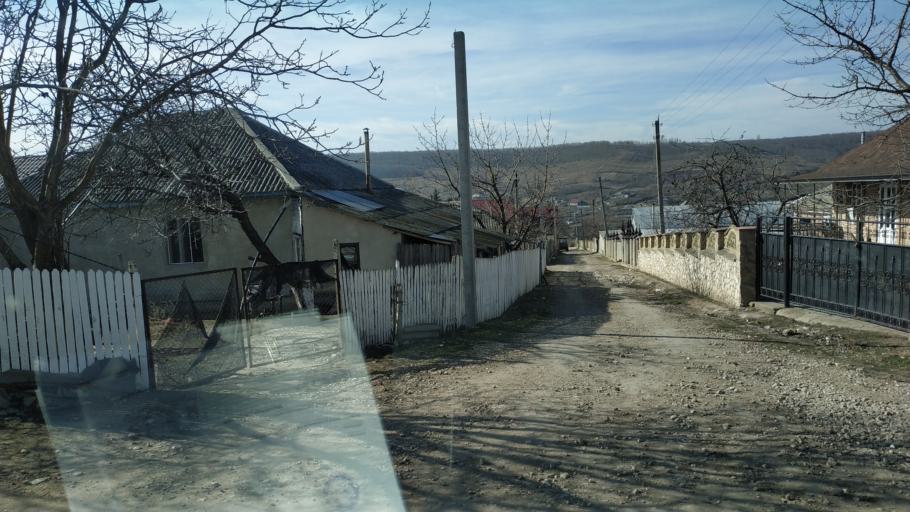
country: MD
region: Chisinau
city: Vatra
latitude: 47.0312
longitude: 28.6320
